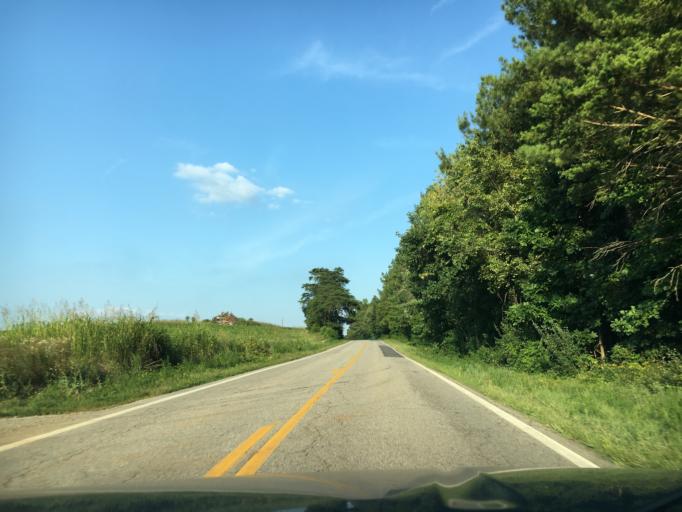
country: US
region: Virginia
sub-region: Pittsylvania County
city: Chatham
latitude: 36.8280
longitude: -79.2952
